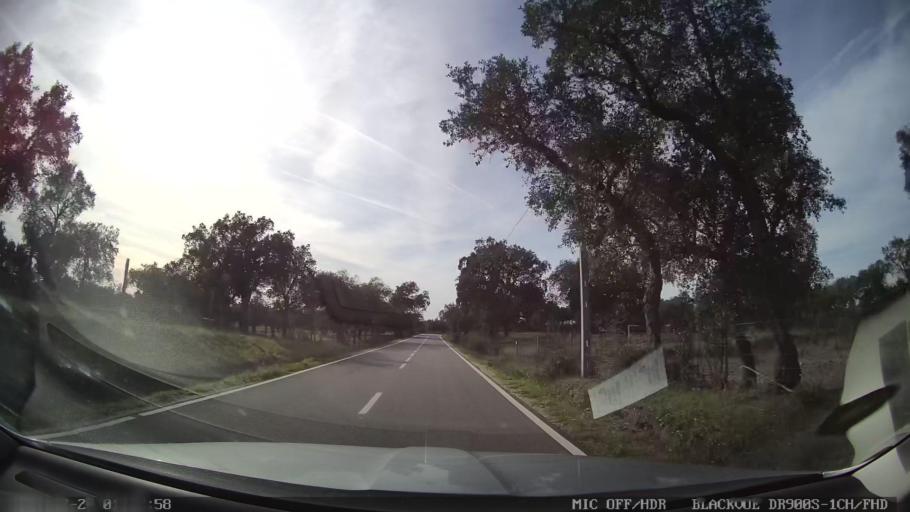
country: PT
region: Portalegre
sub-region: Nisa
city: Nisa
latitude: 39.4559
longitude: -7.7078
